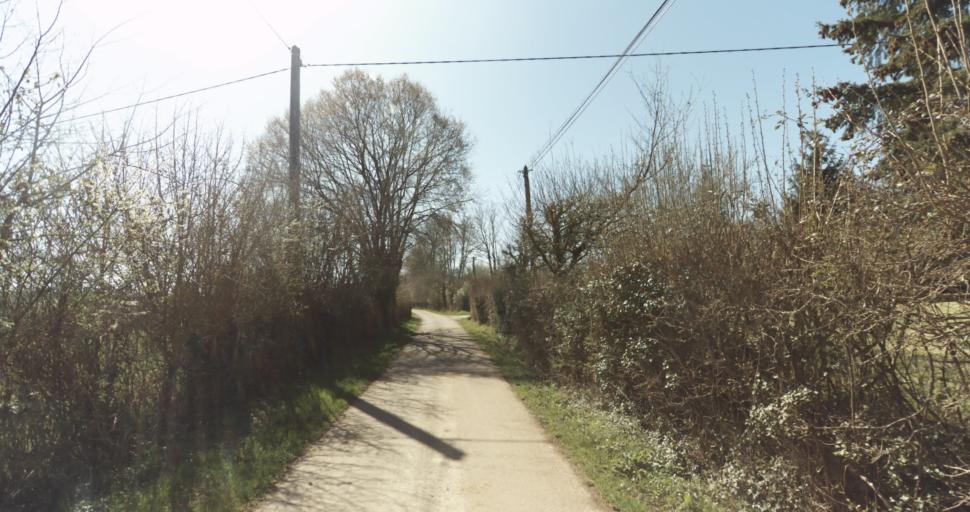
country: FR
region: Lower Normandy
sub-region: Departement du Calvados
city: Saint-Pierre-sur-Dives
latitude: 48.9942
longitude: 0.0569
